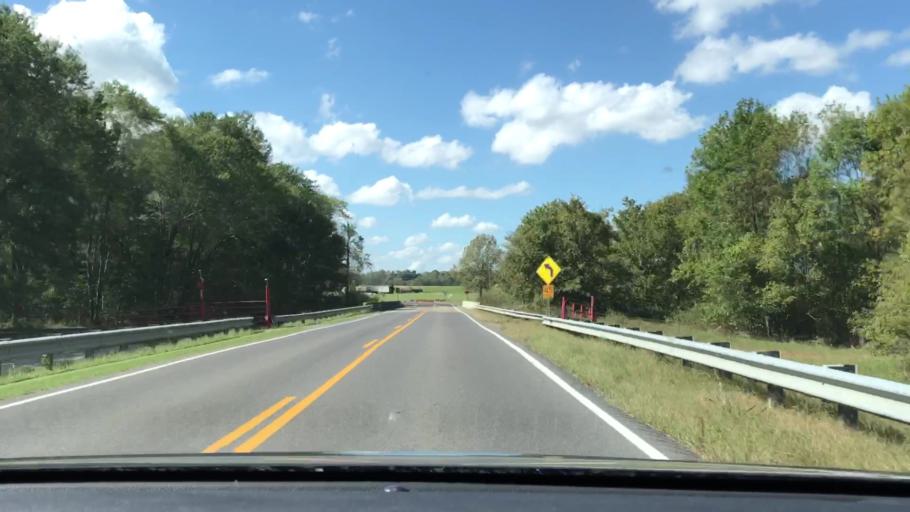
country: US
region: Kentucky
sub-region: McCracken County
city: Reidland
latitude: 36.8845
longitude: -88.5520
